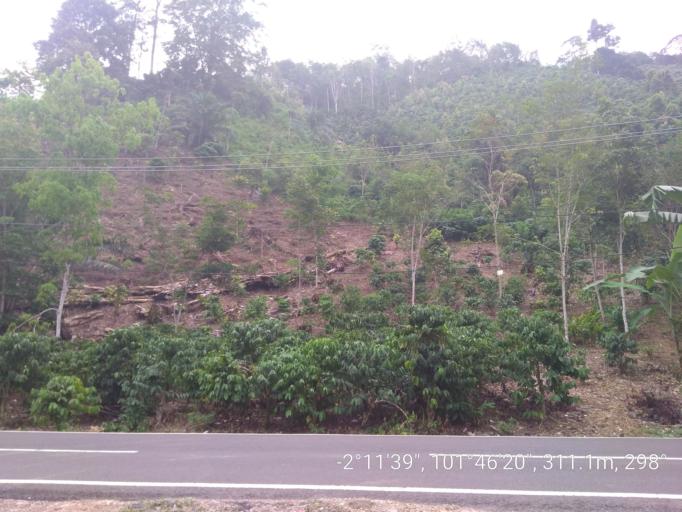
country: ID
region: Jambi
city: Muarasiau
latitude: -2.1944
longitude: 101.7724
